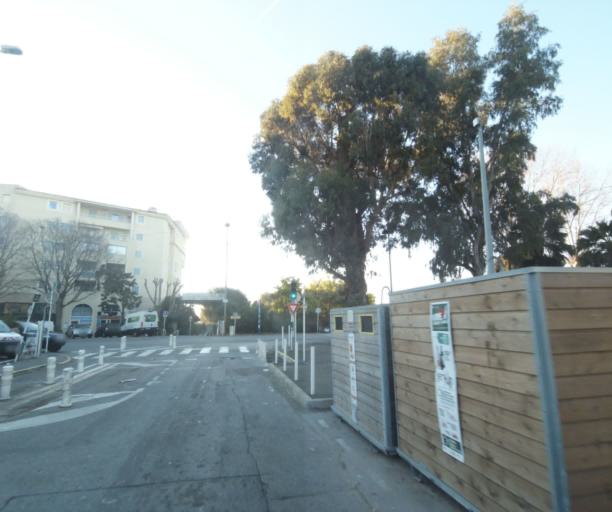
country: FR
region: Provence-Alpes-Cote d'Azur
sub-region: Departement des Alpes-Maritimes
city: Vallauris
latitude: 43.5737
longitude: 7.0873
